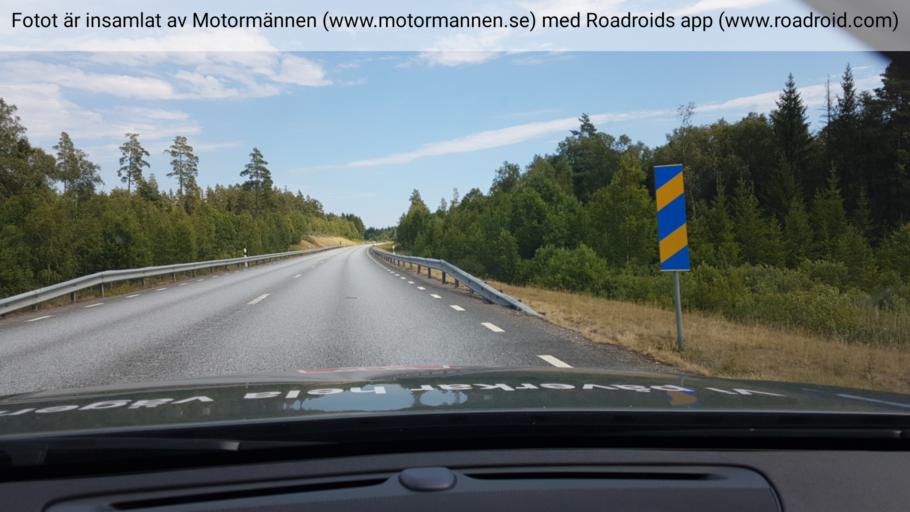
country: SE
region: Uppsala
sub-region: Osthammars Kommun
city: Anneberg
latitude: 60.1729
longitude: 18.3662
